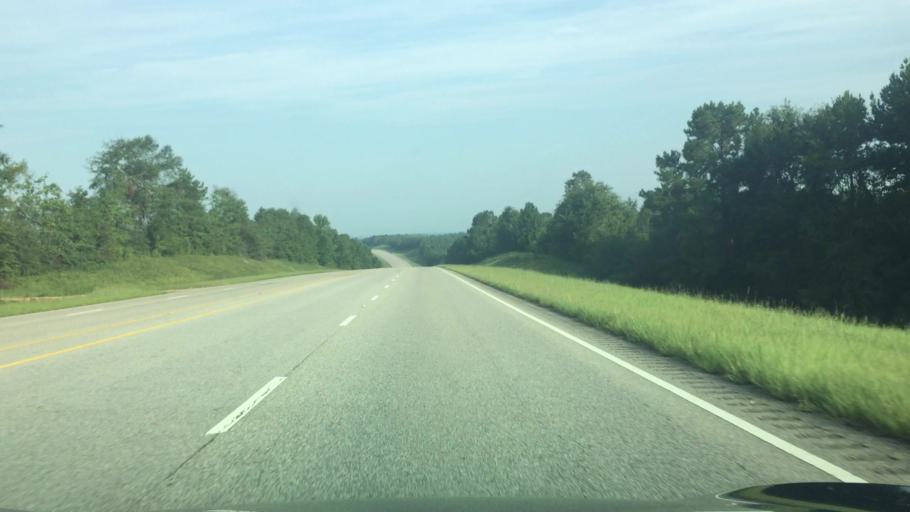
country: US
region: Alabama
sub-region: Covington County
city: Andalusia
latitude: 31.4551
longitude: -86.6337
